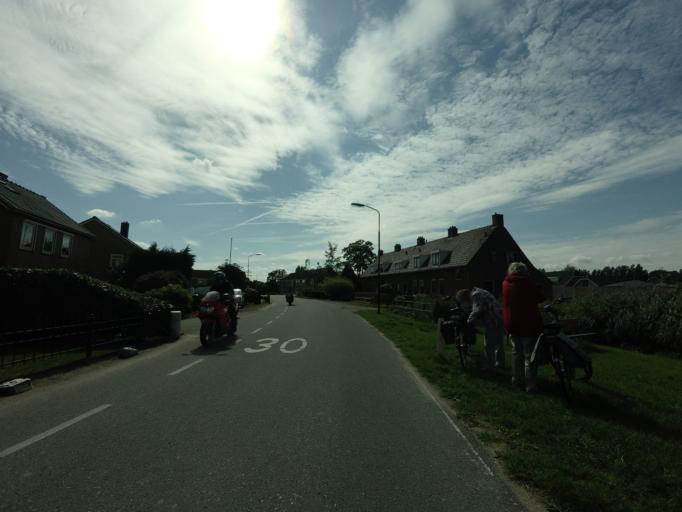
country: NL
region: North Holland
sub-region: Gemeente Uithoorn
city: Uithoorn
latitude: 52.2022
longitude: 4.8146
